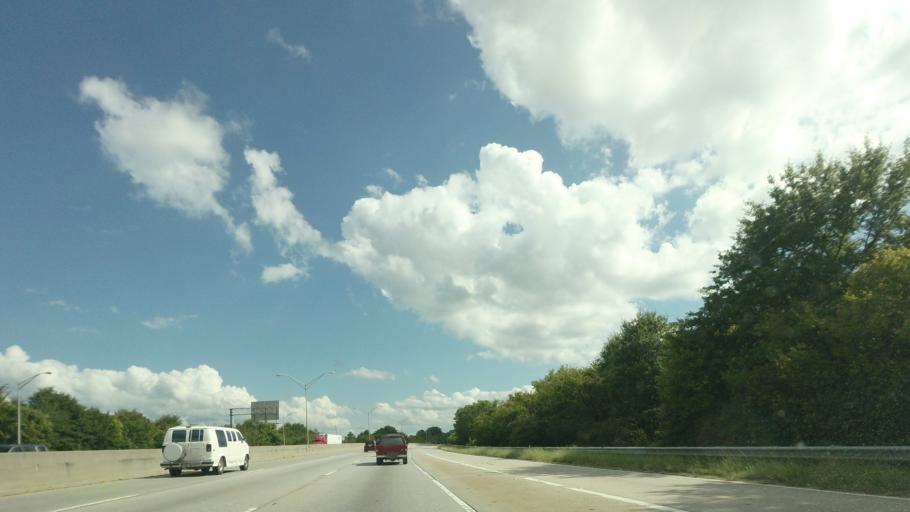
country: US
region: Georgia
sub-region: Bibb County
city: Macon
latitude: 32.8217
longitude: -83.6564
